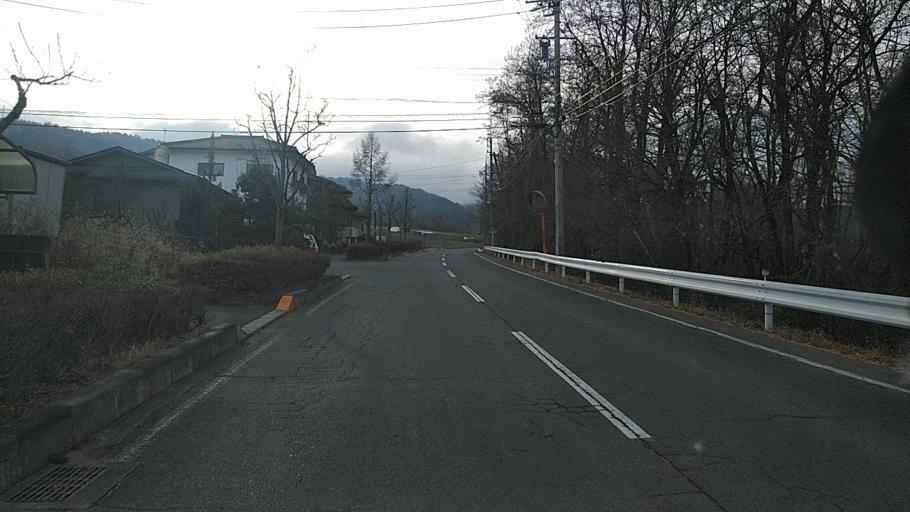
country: JP
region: Nagano
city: Matsumoto
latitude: 36.1787
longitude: 137.9959
